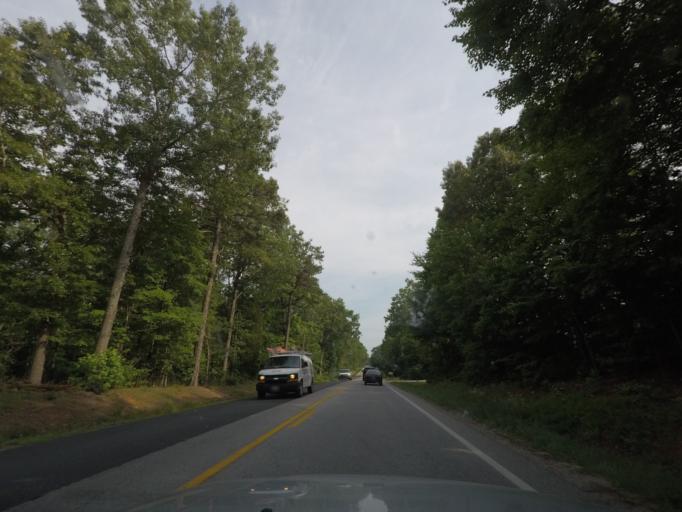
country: US
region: Virginia
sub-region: Prince Edward County
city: Hampden Sydney
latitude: 37.1662
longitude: -78.4404
